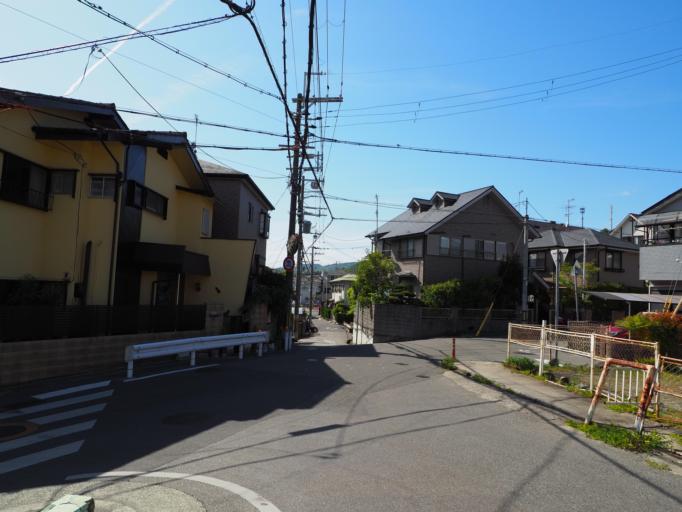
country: JP
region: Hyogo
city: Takarazuka
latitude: 34.8150
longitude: 135.3388
